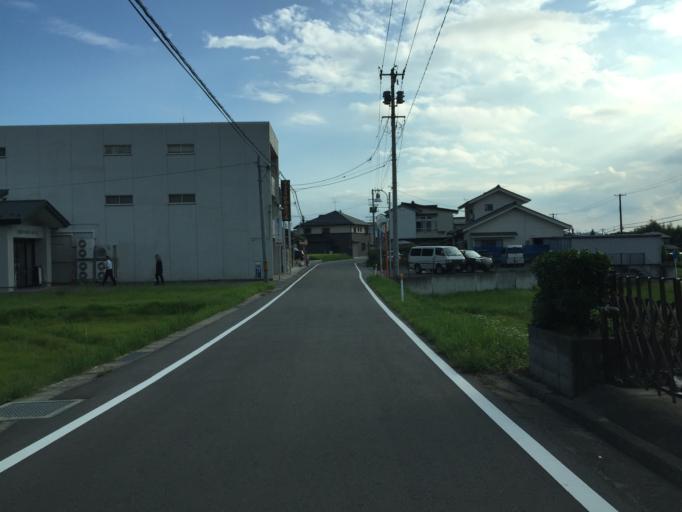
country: JP
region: Fukushima
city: Fukushima-shi
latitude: 37.6598
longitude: 140.5448
